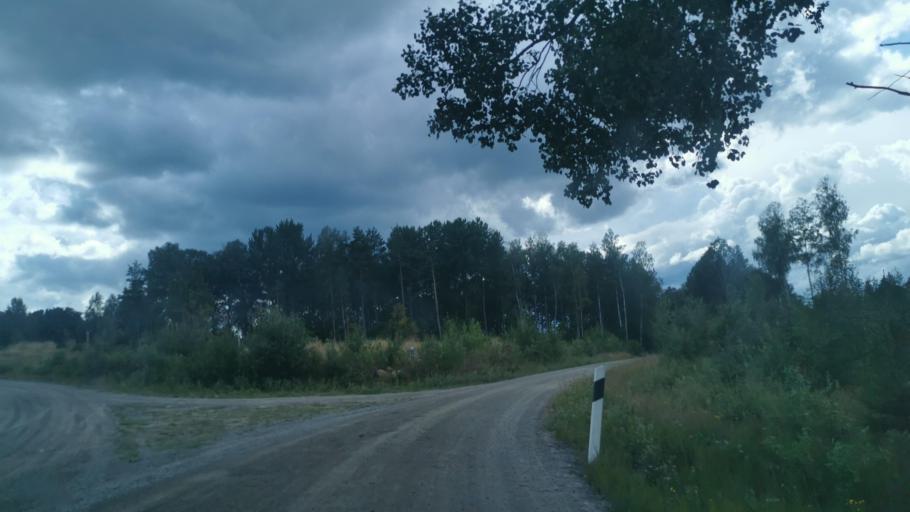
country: SE
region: OEstergoetland
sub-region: Finspangs Kommun
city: Finspang
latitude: 58.7936
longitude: 15.7723
